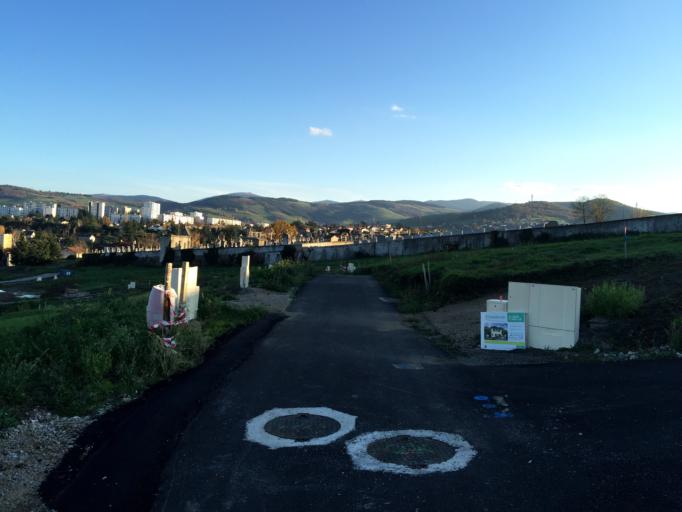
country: FR
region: Rhone-Alpes
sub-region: Departement de la Loire
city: Saint-Chamond
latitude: 45.4820
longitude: 4.5187
